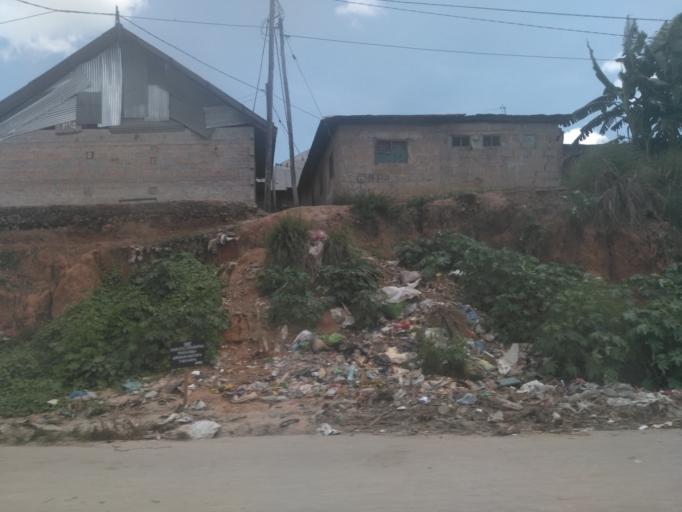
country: TZ
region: Zanzibar Urban/West
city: Zanzibar
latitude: -6.1409
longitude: 39.2209
